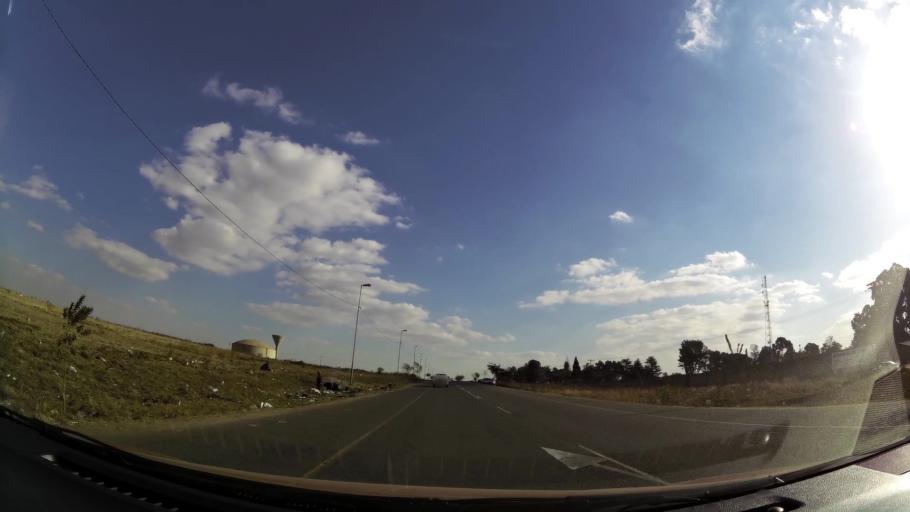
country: ZA
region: Gauteng
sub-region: City of Johannesburg Metropolitan Municipality
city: Midrand
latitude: -26.0106
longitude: 28.1673
